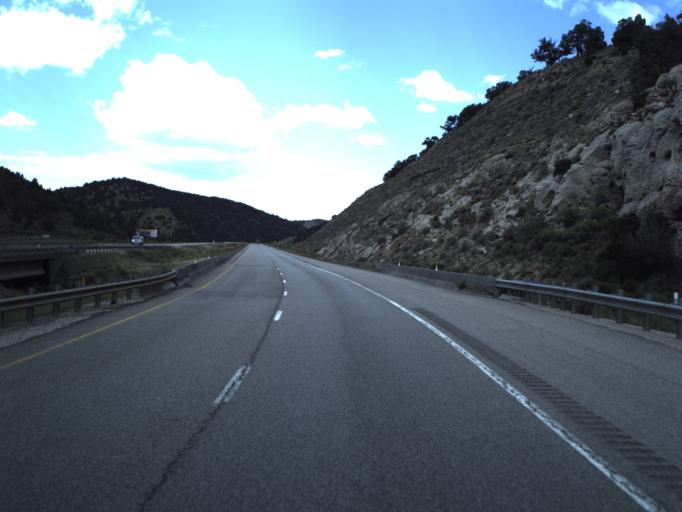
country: US
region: Utah
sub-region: Wayne County
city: Loa
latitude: 38.7596
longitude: -111.4511
